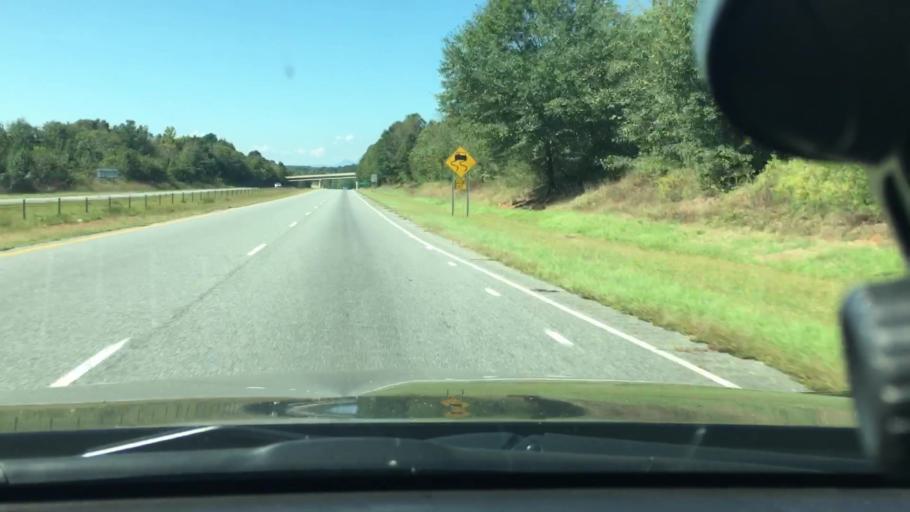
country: US
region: North Carolina
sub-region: Rutherford County
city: Forest City
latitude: 35.3115
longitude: -81.8825
